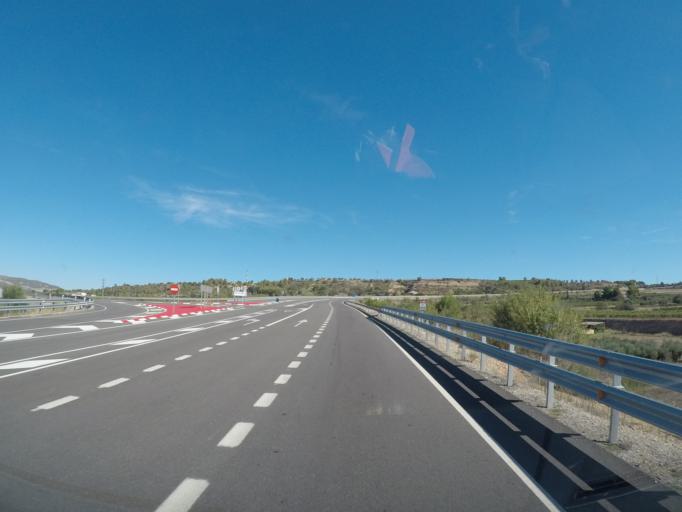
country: ES
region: Catalonia
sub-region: Provincia de Tarragona
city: Garcia
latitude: 41.1005
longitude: 0.6602
